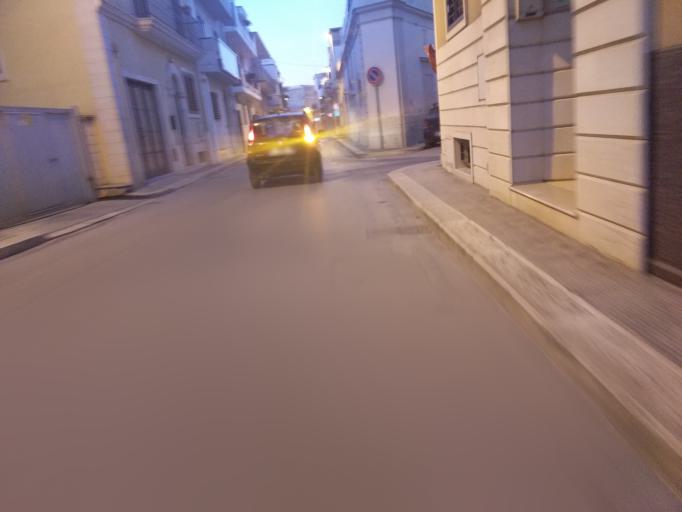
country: IT
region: Apulia
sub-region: Provincia di Bari
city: Modugno
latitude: 41.0795
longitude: 16.7806
